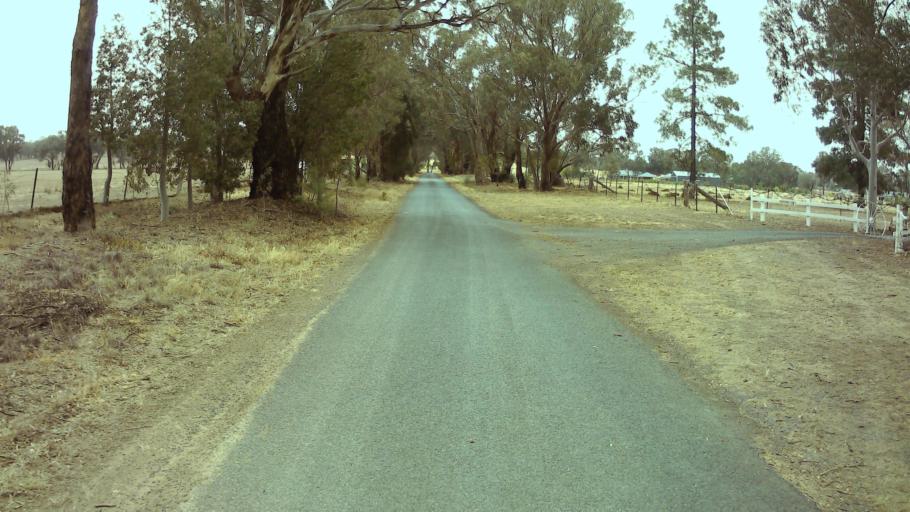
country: AU
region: New South Wales
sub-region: Weddin
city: Grenfell
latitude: -33.8987
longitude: 148.1428
